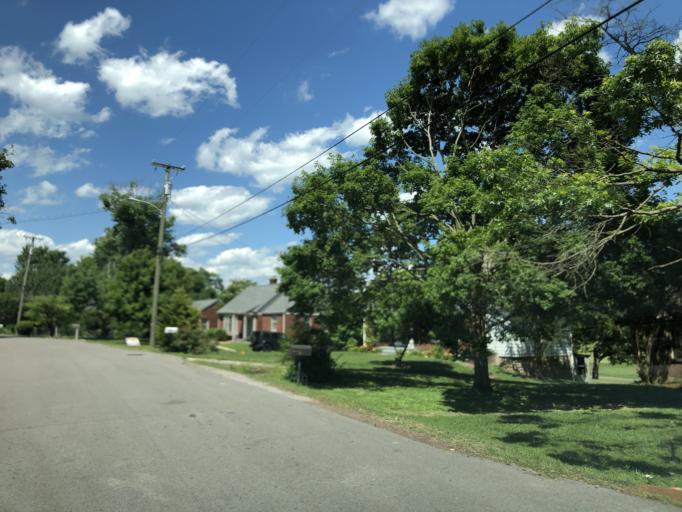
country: US
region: Tennessee
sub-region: Davidson County
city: Nashville
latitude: 36.1784
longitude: -86.7298
